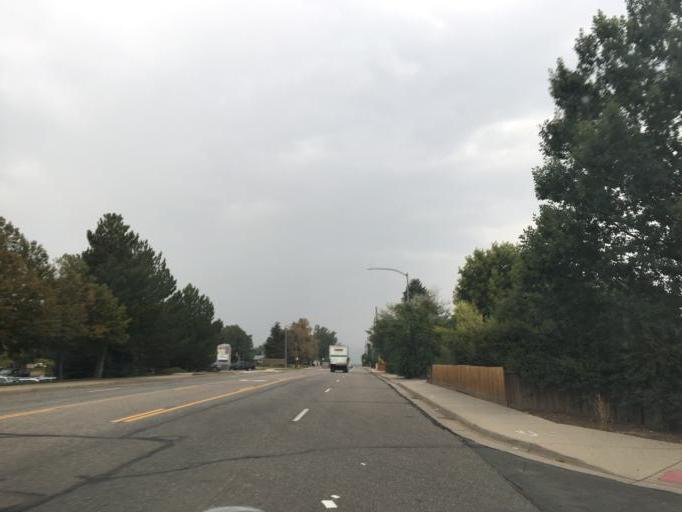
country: US
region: Colorado
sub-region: Jefferson County
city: Wheat Ridge
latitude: 39.7694
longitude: -105.0905
